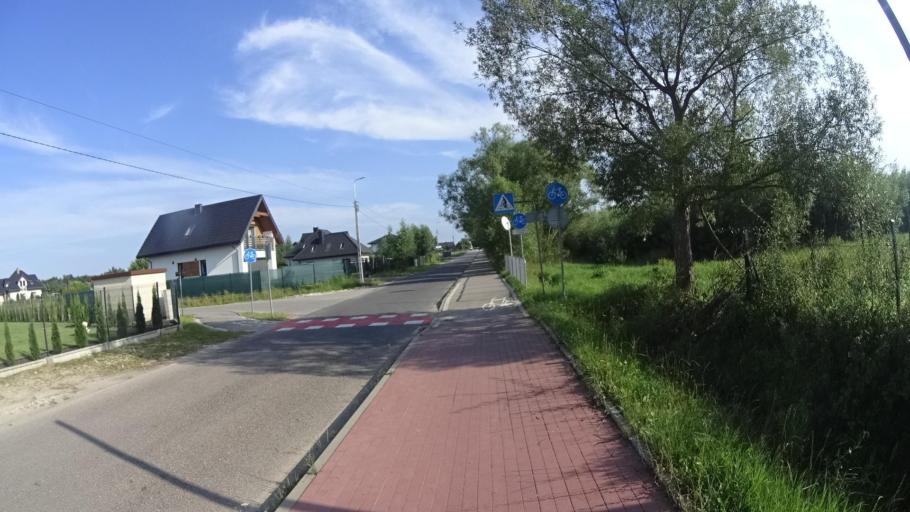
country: PL
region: Masovian Voivodeship
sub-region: Powiat pruszkowski
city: Nadarzyn
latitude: 52.0665
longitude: 20.7880
